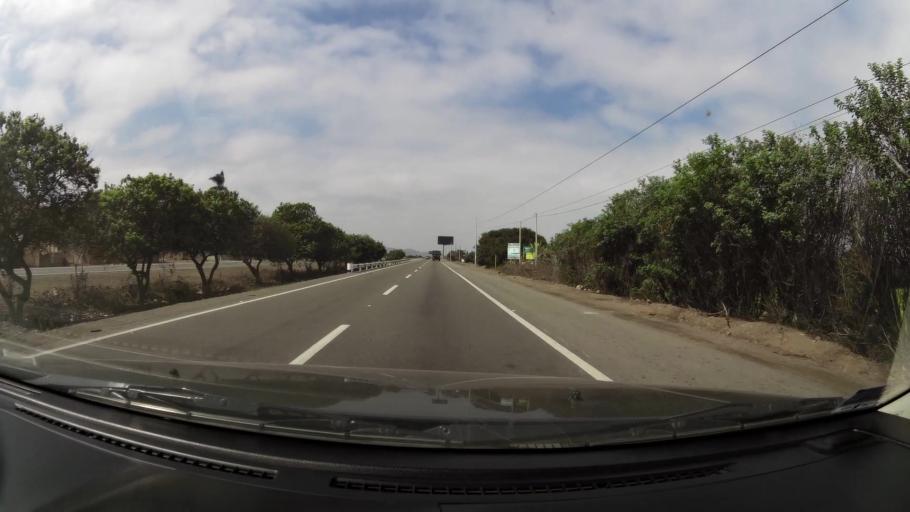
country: PE
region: Lima
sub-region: Provincia de Canete
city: Mala
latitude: -12.6651
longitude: -76.6580
